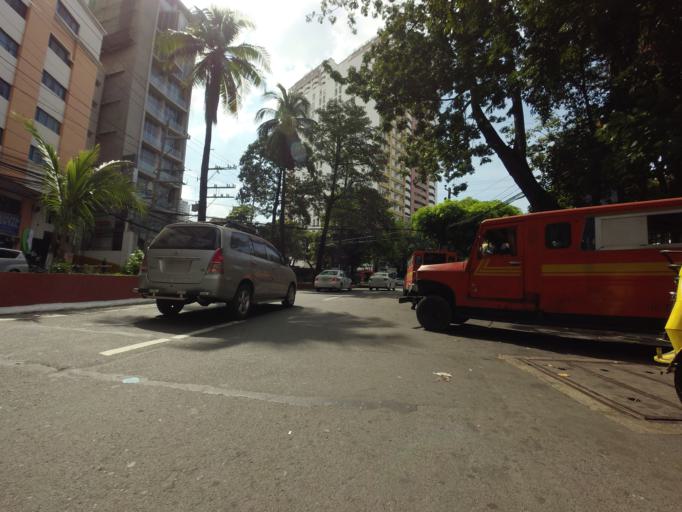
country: PH
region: Metro Manila
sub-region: City of Manila
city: Port Area
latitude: 14.5615
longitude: 120.9941
